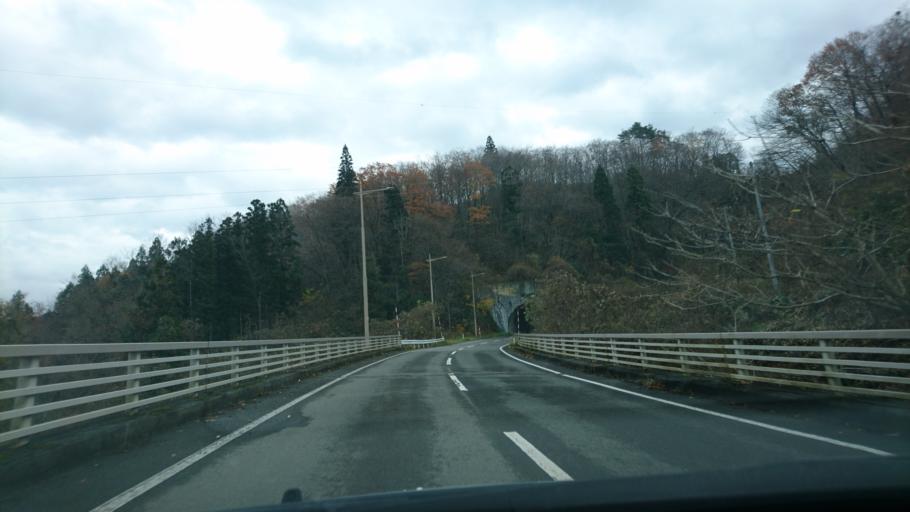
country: JP
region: Iwate
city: Ichinoseki
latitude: 38.9040
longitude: 140.9023
